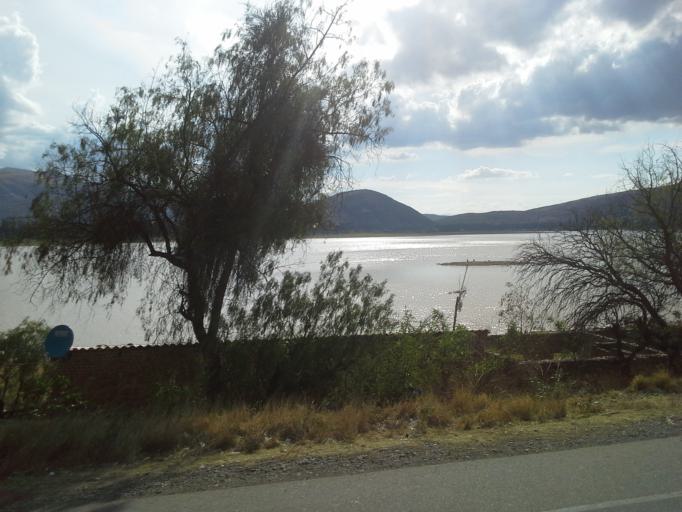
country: BO
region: Cochabamba
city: Tarata
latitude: -17.5343
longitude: -66.0824
